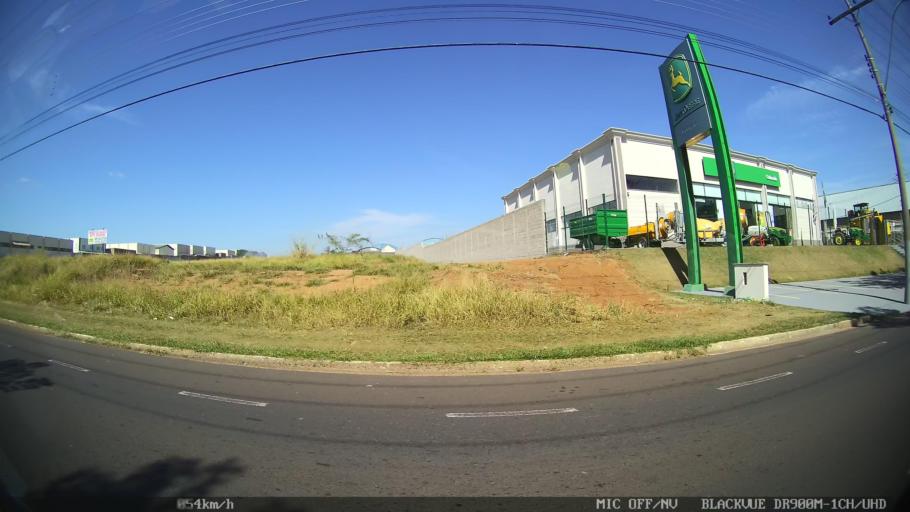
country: BR
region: Sao Paulo
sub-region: Franca
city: Franca
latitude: -20.5467
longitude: -47.4325
